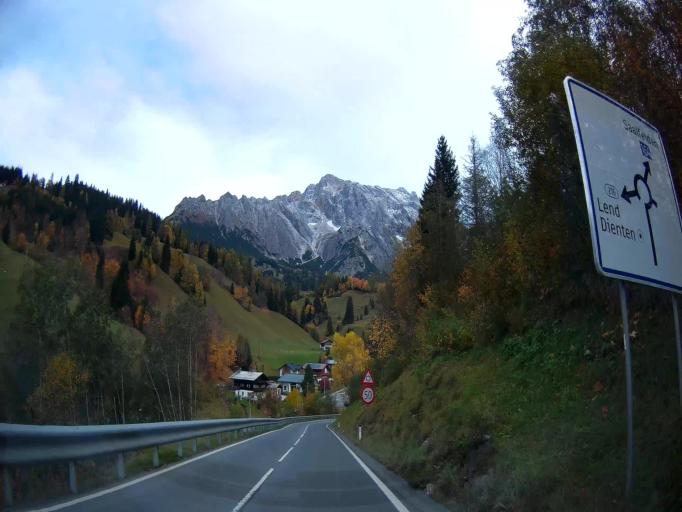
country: AT
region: Salzburg
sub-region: Politischer Bezirk Zell am See
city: Dienten am Hochkonig
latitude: 47.3874
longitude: 13.0109
